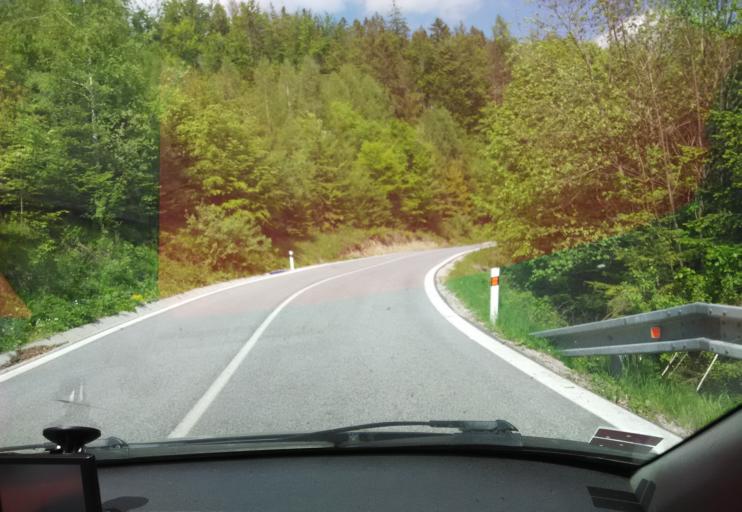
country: SK
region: Kosicky
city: Dobsina
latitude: 48.8500
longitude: 20.4664
